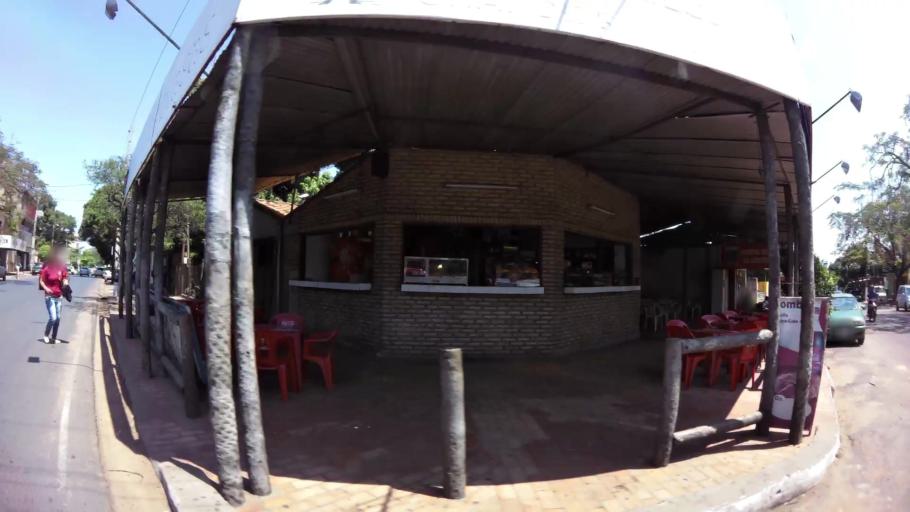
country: PY
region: Central
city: San Lorenzo
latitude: -25.3478
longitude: -57.5073
